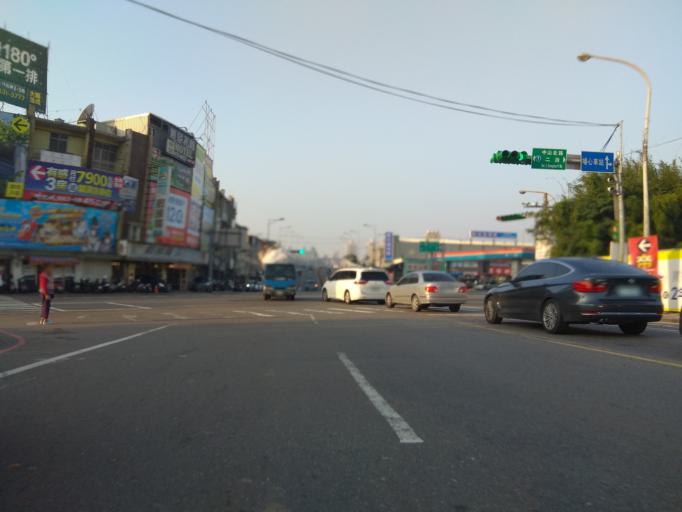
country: TW
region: Taiwan
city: Daxi
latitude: 24.9112
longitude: 121.1745
